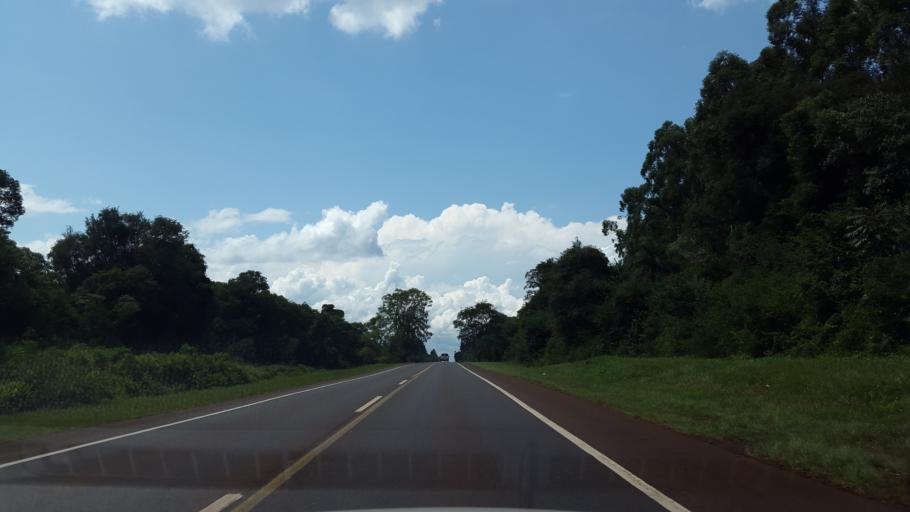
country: AR
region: Misiones
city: El Alcazar
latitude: -26.7047
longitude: -54.8422
